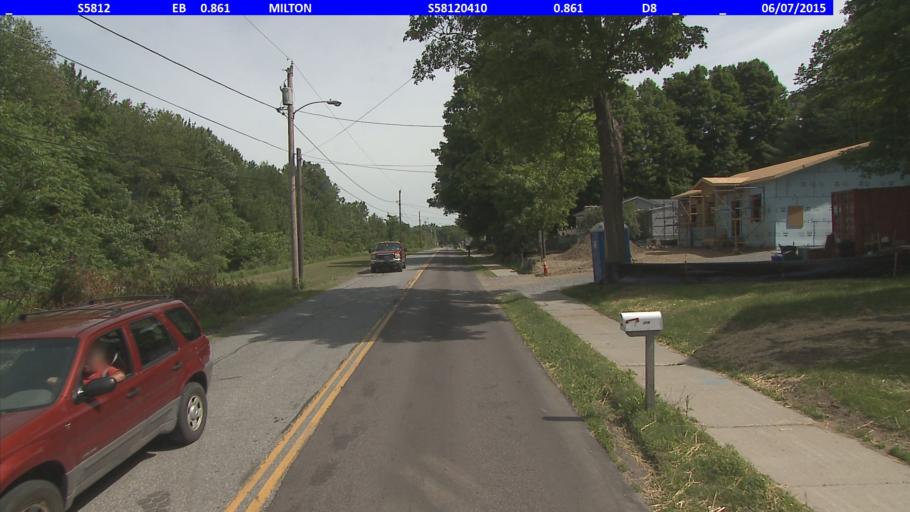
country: US
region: Vermont
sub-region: Chittenden County
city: Milton
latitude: 44.6310
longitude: -73.1072
